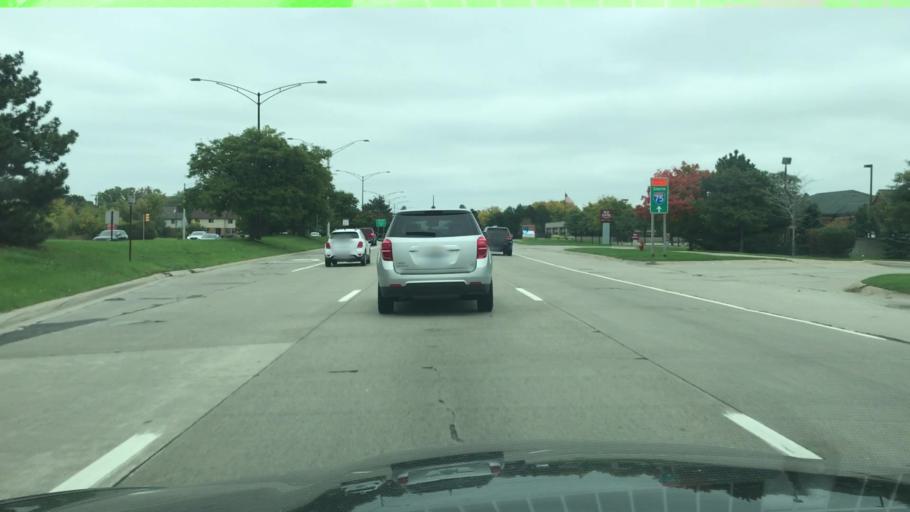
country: US
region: Michigan
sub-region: Oakland County
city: Clawson
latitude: 42.5635
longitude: -83.1071
